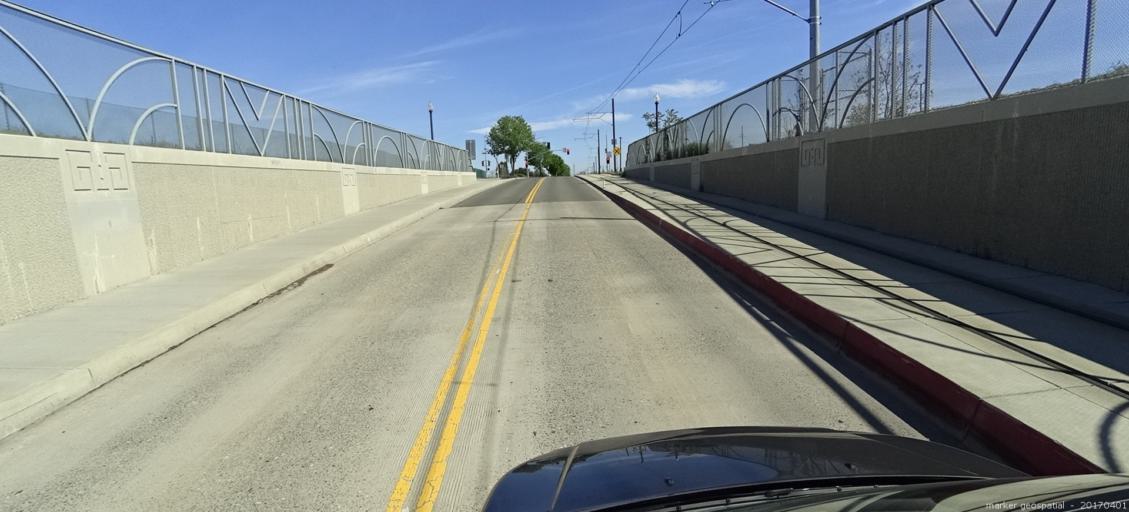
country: US
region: California
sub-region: Sacramento County
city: Sacramento
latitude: 38.5884
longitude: -121.4946
